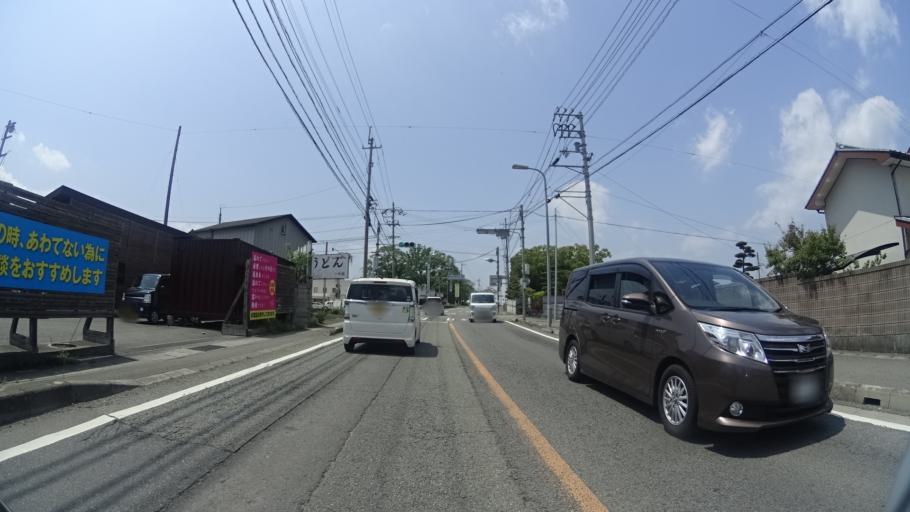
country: JP
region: Tokushima
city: Kamojimacho-jogejima
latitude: 34.0651
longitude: 134.3261
